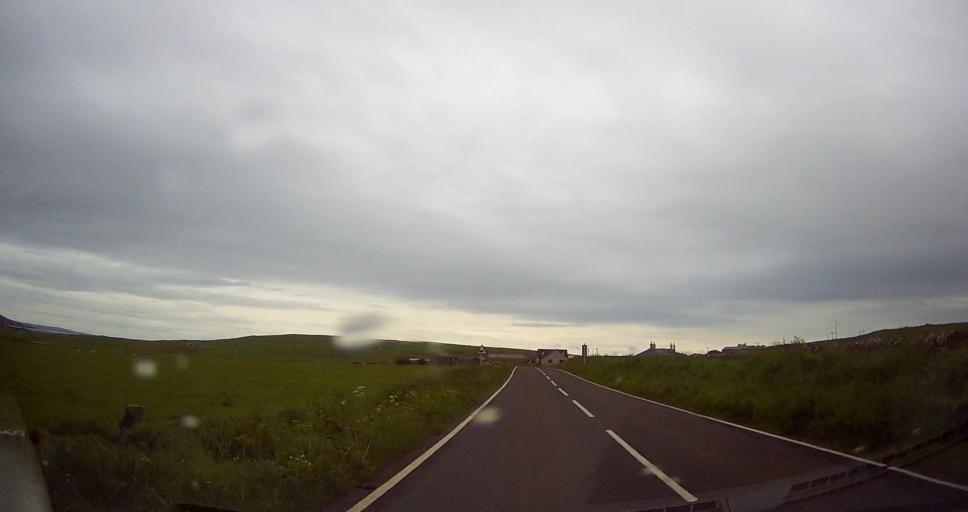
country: GB
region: Scotland
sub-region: Orkney Islands
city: Orkney
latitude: 59.1118
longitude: -3.1032
